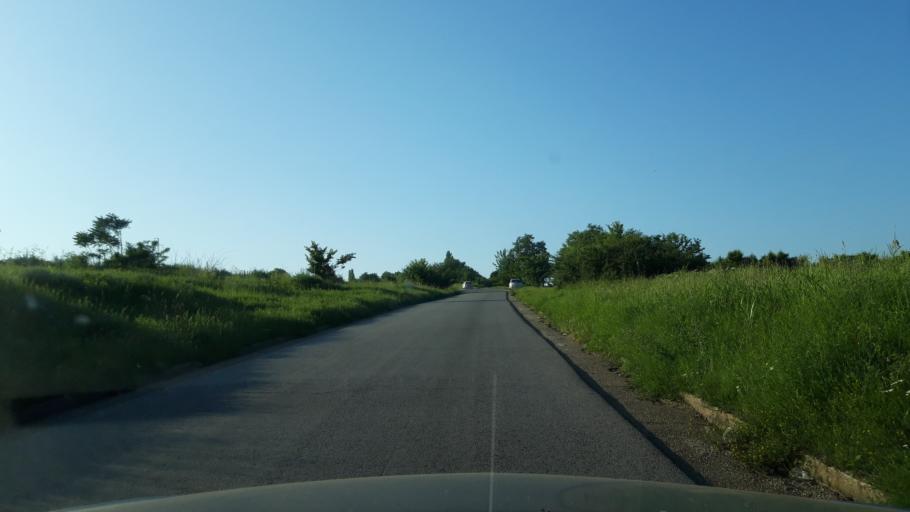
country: RS
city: Celarevo
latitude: 45.1279
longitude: 19.5075
